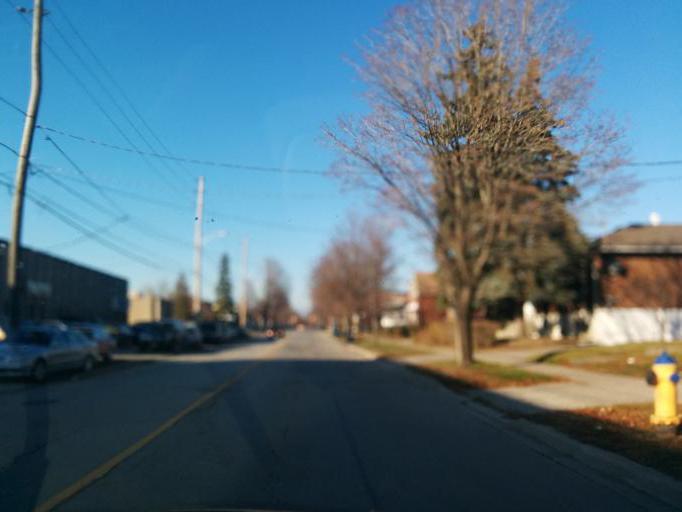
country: CA
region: Ontario
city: Etobicoke
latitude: 43.6015
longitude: -79.5324
